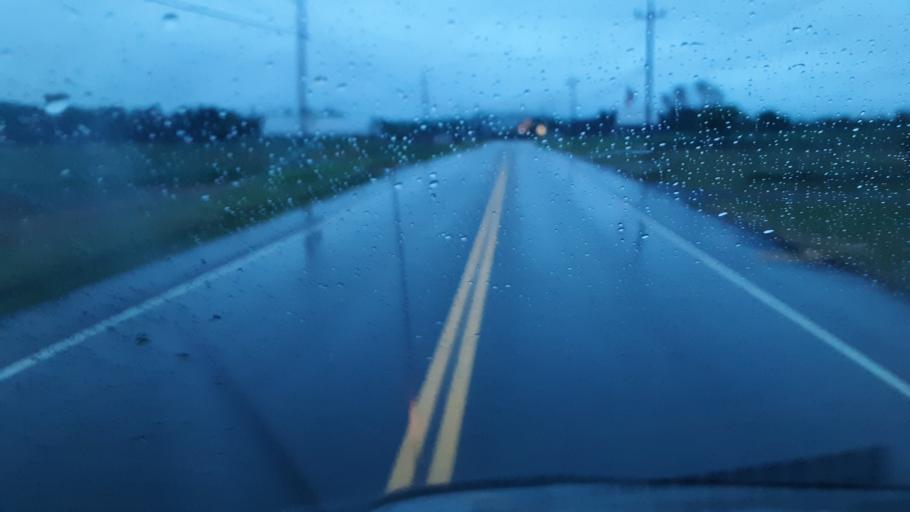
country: US
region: Maine
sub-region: Penobscot County
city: Patten
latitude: 45.9089
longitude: -68.4364
